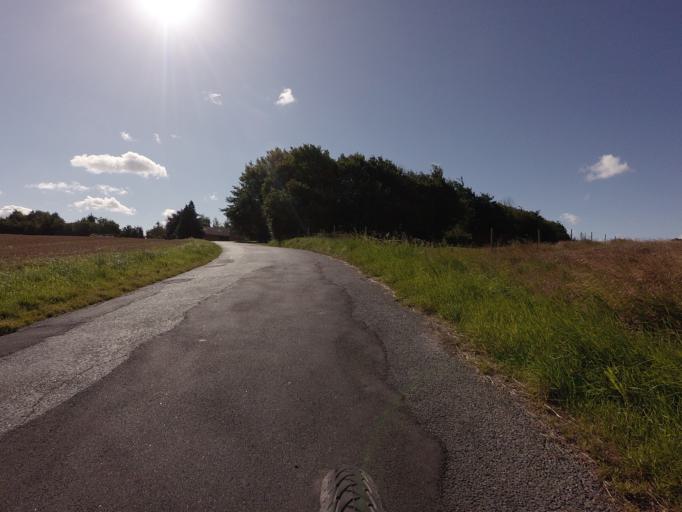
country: DK
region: Central Jutland
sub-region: Horsens Kommune
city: Braedstrup
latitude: 55.9713
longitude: 9.7134
